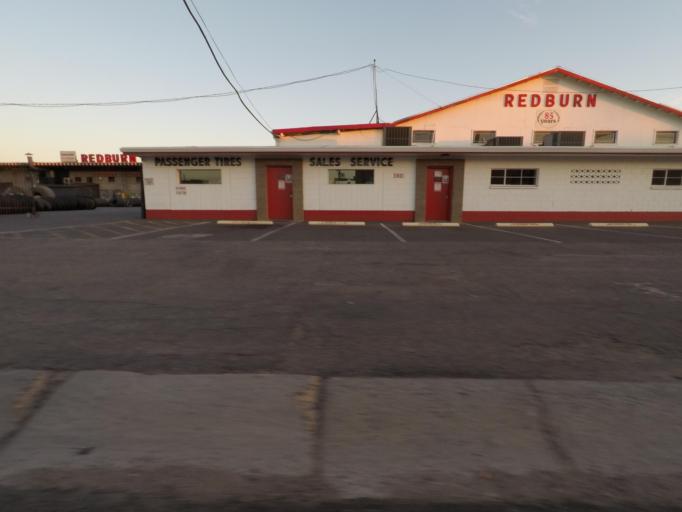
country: US
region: Arizona
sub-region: Maricopa County
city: Glendale
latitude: 33.4922
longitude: -112.1402
